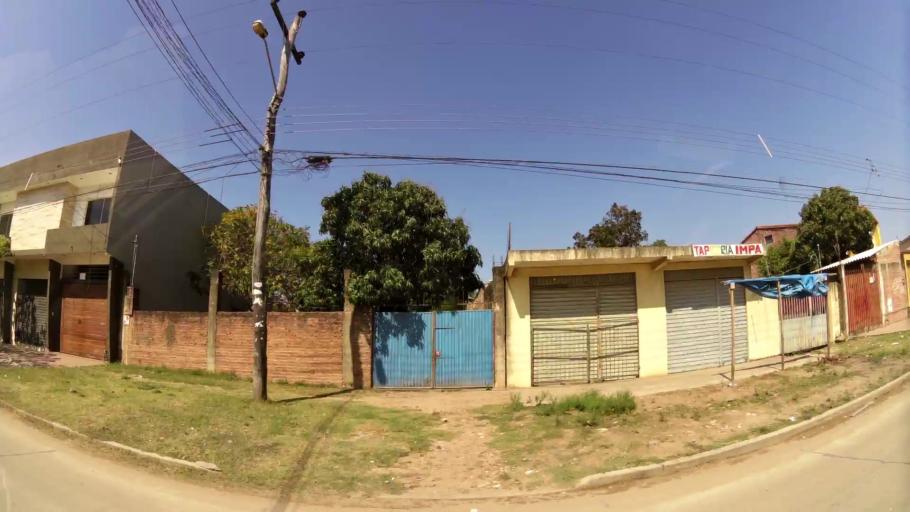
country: BO
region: Santa Cruz
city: Santa Cruz de la Sierra
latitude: -17.7477
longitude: -63.1464
